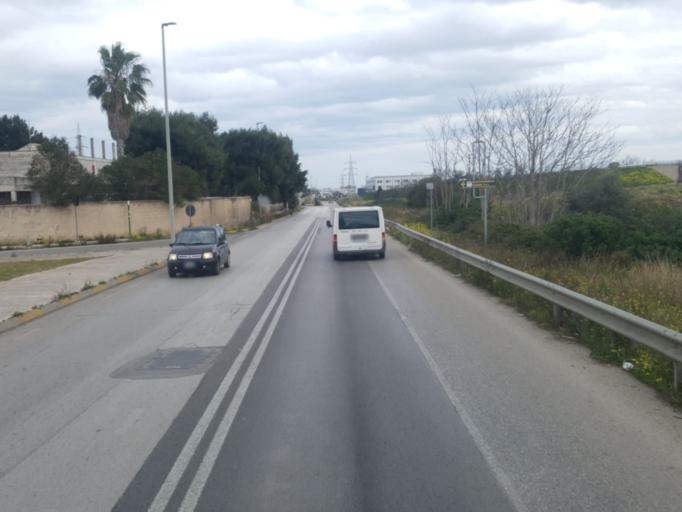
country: IT
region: Apulia
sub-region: Provincia di Bari
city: Modugno
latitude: 41.1029
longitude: 16.8024
